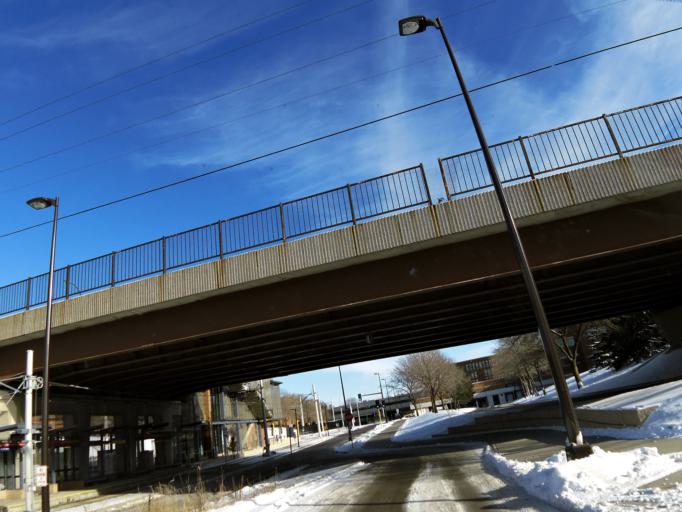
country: US
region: Minnesota
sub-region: Hennepin County
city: Minneapolis
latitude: 44.9718
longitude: -93.2460
